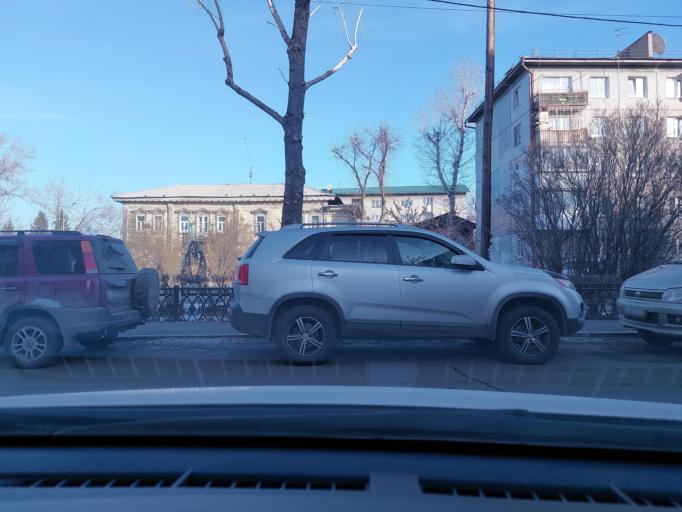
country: RU
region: Irkutsk
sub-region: Irkutskiy Rayon
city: Irkutsk
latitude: 52.2900
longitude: 104.2763
